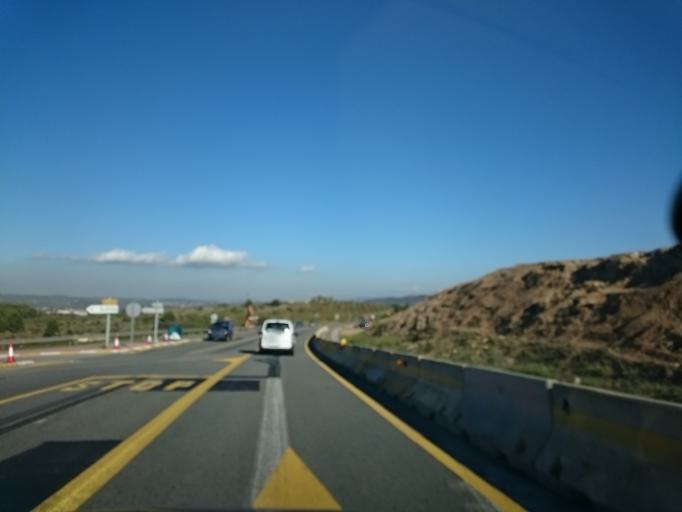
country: ES
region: Catalonia
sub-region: Provincia de Barcelona
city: Sant Llorenc d'Hortons
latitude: 41.4804
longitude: 1.8674
